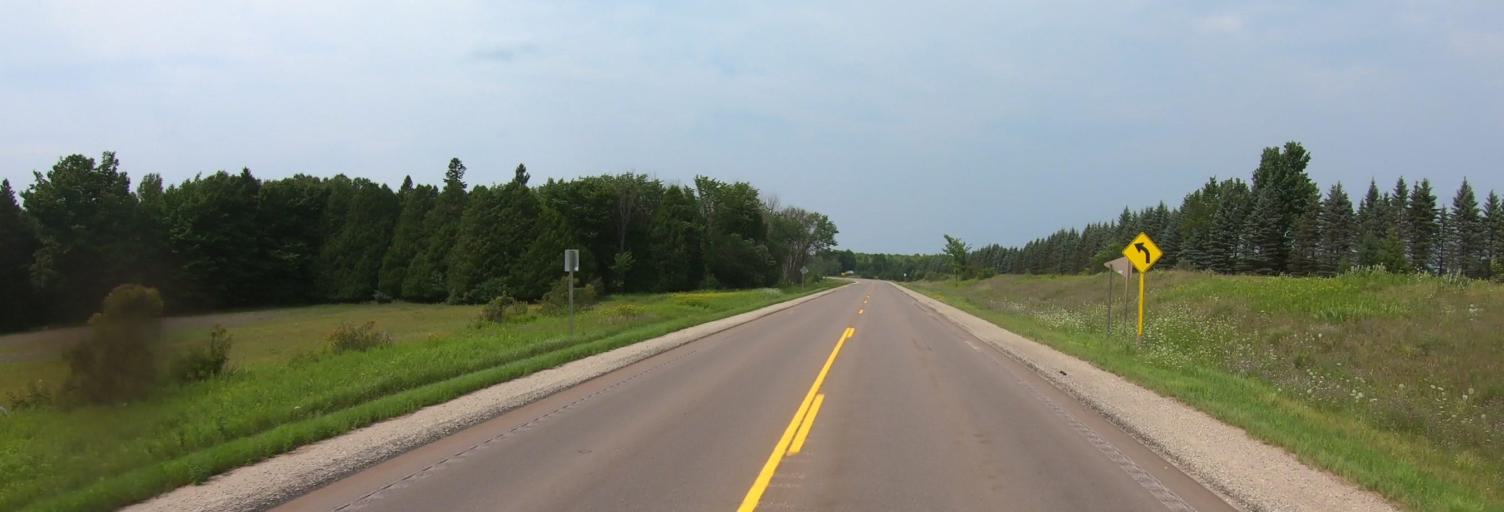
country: US
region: Michigan
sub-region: Alger County
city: Munising
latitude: 46.3505
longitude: -86.9517
